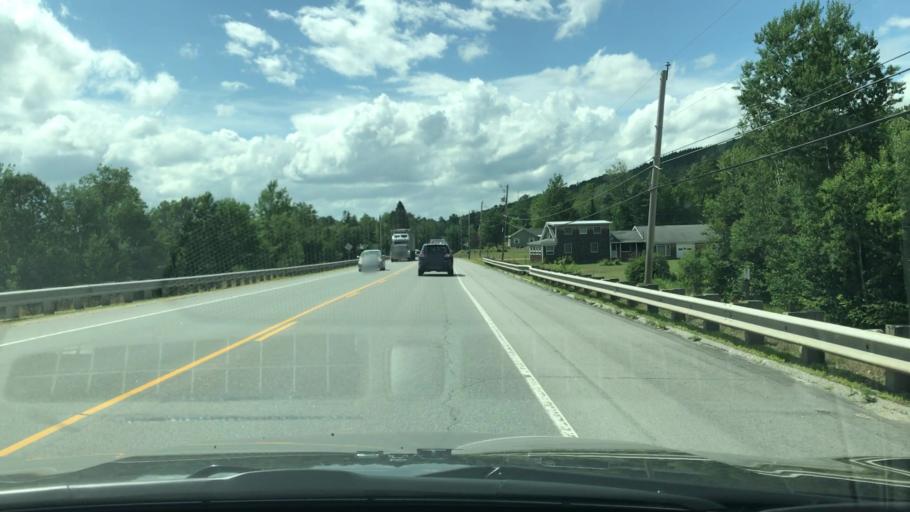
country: US
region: New Hampshire
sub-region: Coos County
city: Jefferson
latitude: 44.3592
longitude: -71.3668
